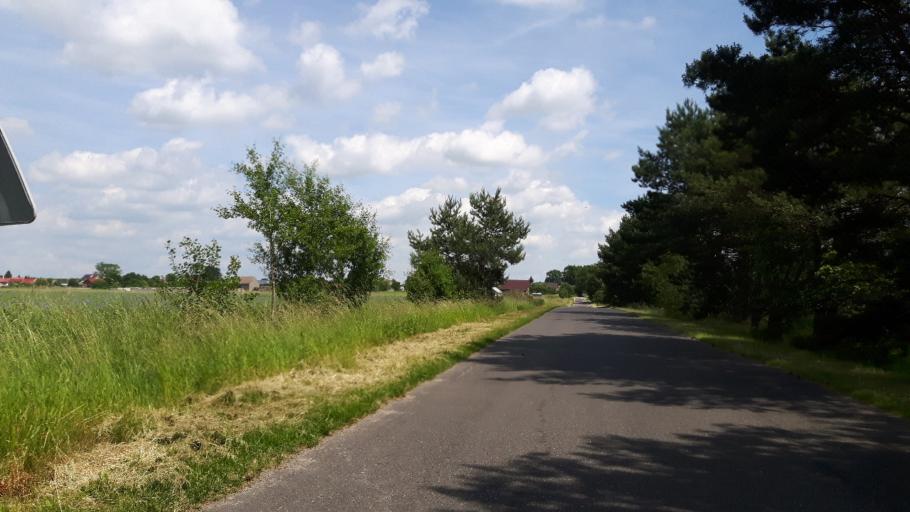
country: PL
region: West Pomeranian Voivodeship
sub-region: Powiat goleniowski
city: Osina
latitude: 53.6541
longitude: 14.9676
